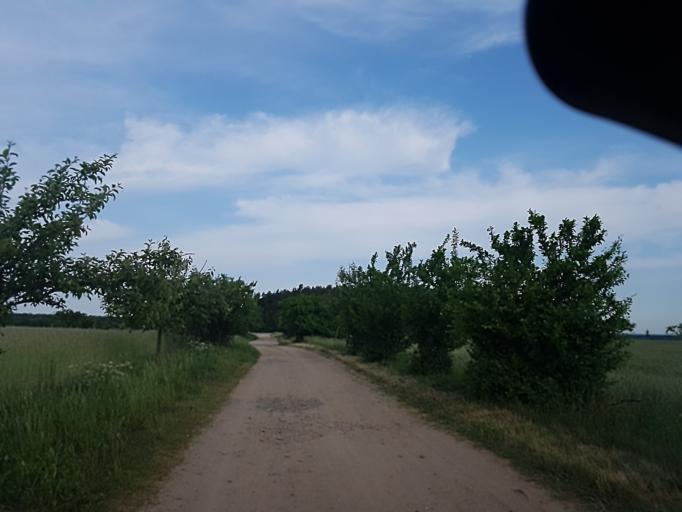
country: DE
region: Brandenburg
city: Niemegk
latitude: 52.0474
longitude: 12.6933
